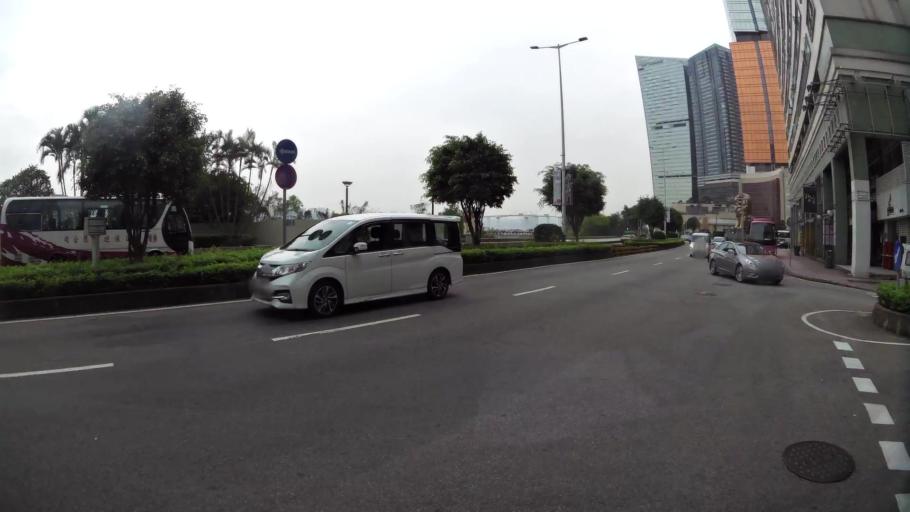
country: MO
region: Macau
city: Macau
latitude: 22.1860
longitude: 113.5503
